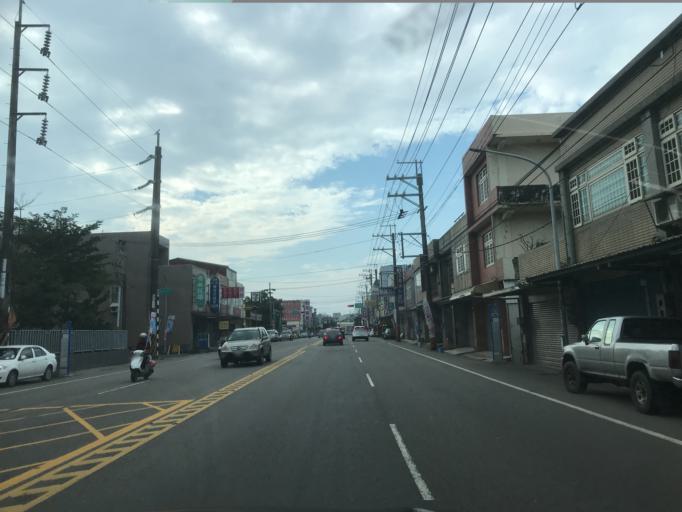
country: TW
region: Taiwan
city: Daxi
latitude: 24.9029
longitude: 121.2700
